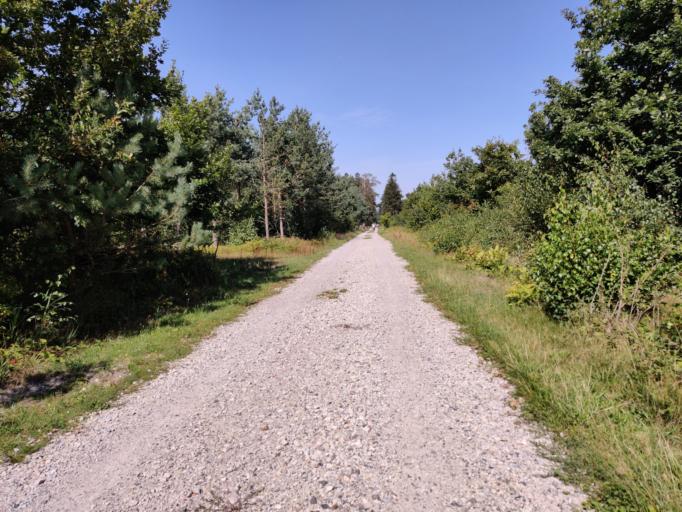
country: DK
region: Zealand
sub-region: Guldborgsund Kommune
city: Nykobing Falster
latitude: 54.6254
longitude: 11.9574
